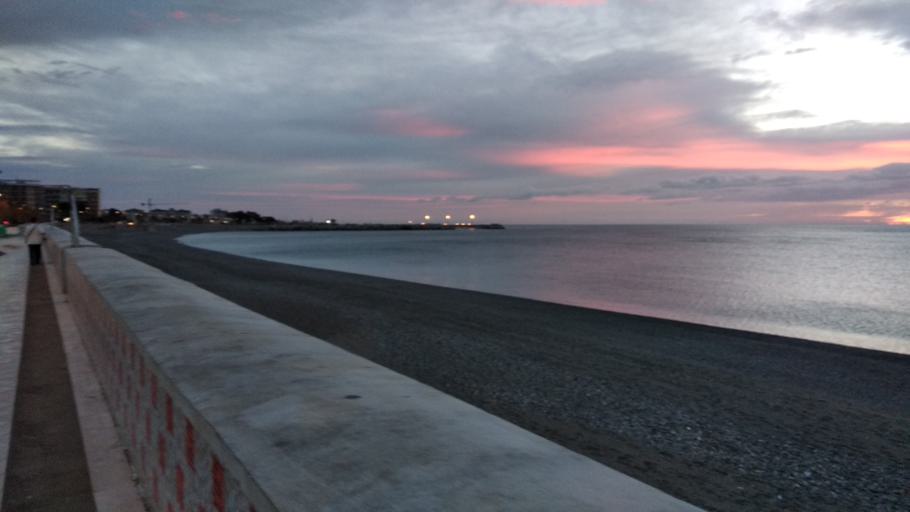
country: IT
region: Calabria
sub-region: Provincia di Catanzaro
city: Roccelletta
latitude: 38.8244
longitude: 16.6222
